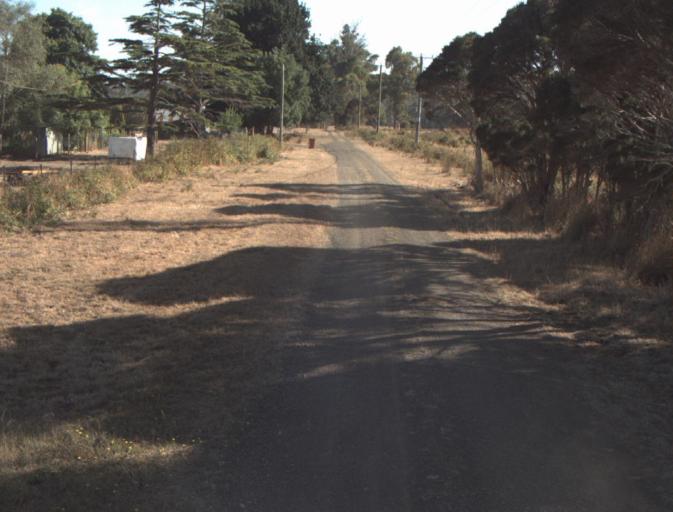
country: AU
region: Tasmania
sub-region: Dorset
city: Bridport
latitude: -41.1437
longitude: 147.2122
